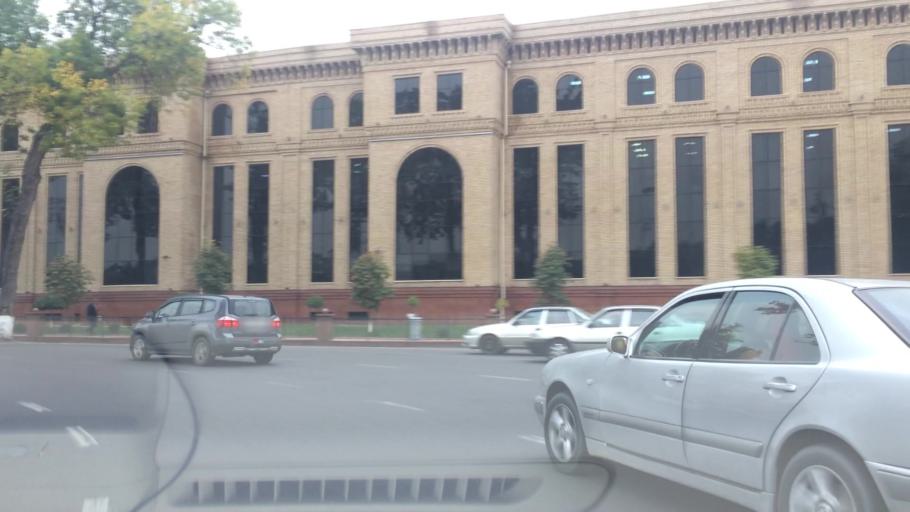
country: UZ
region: Toshkent Shahri
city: Tashkent
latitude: 41.3106
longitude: 69.2778
